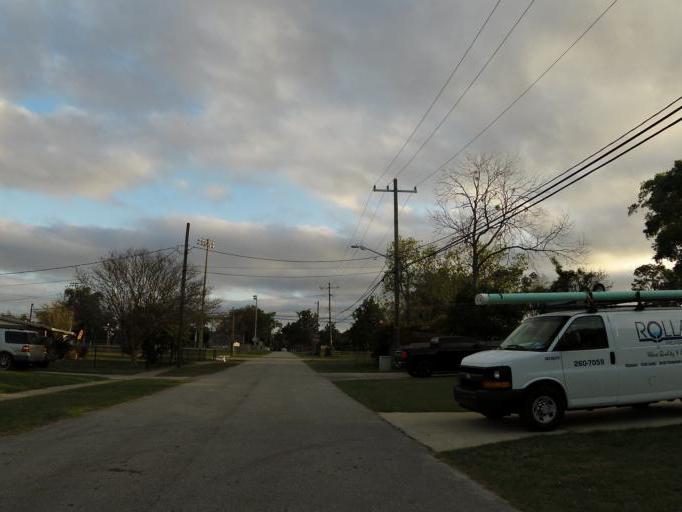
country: US
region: Florida
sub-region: Duval County
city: Jacksonville
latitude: 30.4402
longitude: -81.6297
